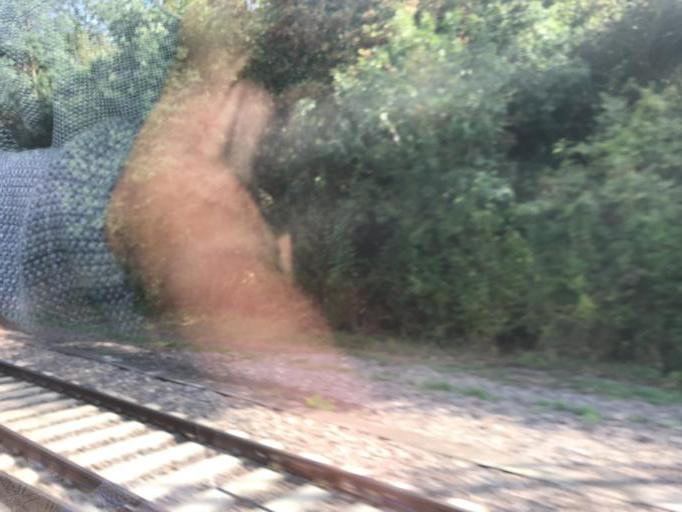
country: DE
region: Saarland
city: Neunkirchen
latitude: 49.3577
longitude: 7.1783
